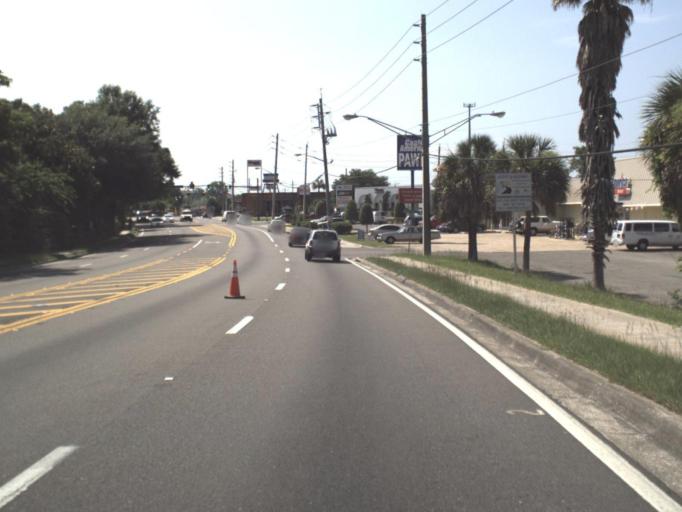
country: US
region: Florida
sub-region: Duval County
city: Jacksonville
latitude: 30.3942
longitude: -81.6822
